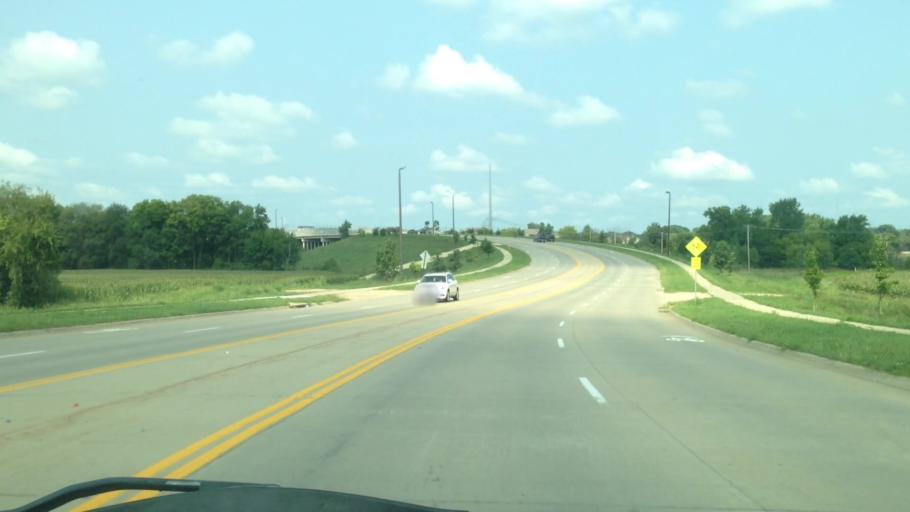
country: US
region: Iowa
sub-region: Linn County
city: Cedar Rapids
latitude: 41.9440
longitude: -91.6902
